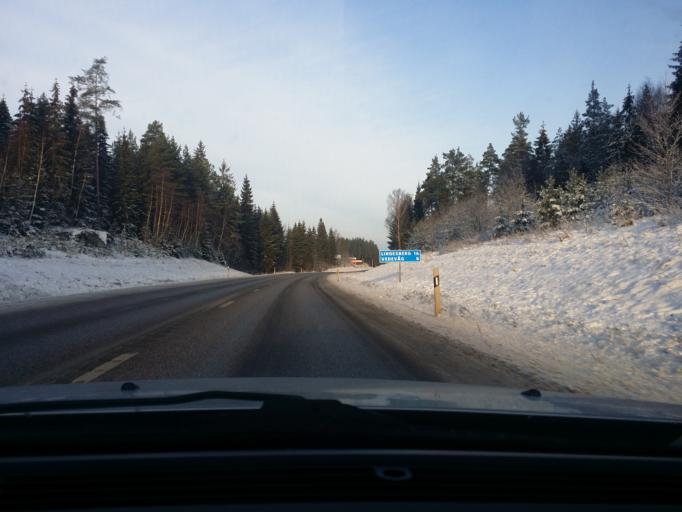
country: SE
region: OErebro
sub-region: Lindesbergs Kommun
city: Frovi
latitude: 59.4820
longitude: 15.3785
